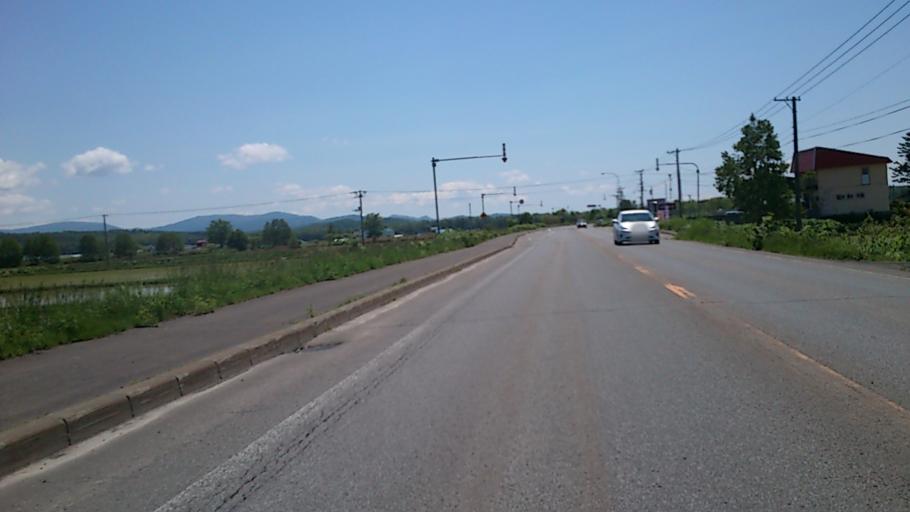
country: JP
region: Hokkaido
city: Nayoro
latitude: 44.3181
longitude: 142.4572
